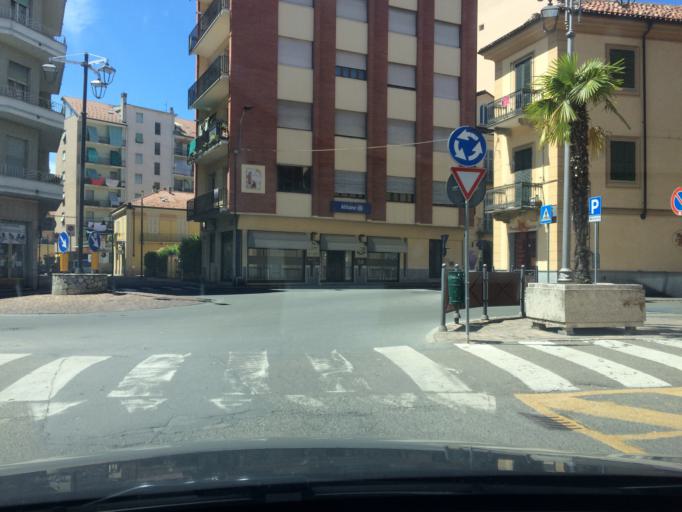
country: IT
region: Piedmont
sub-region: Provincia di Alessandria
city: Acqui Terme
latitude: 44.6739
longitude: 8.4666
